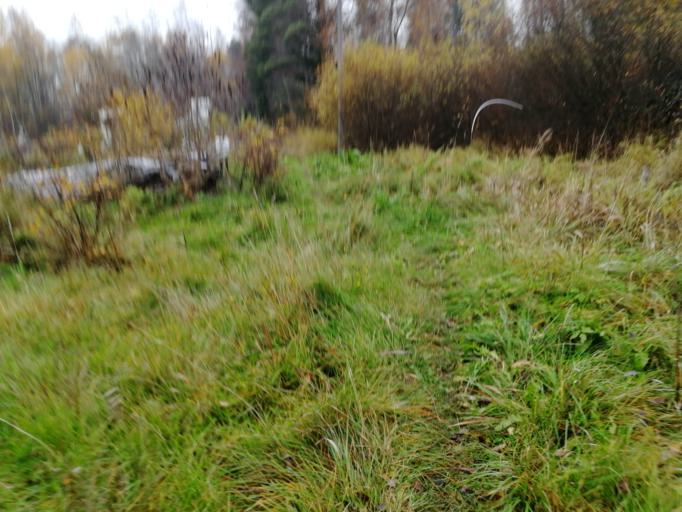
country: FI
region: Pirkanmaa
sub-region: Tampere
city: Tampere
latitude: 61.4500
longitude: 23.8882
